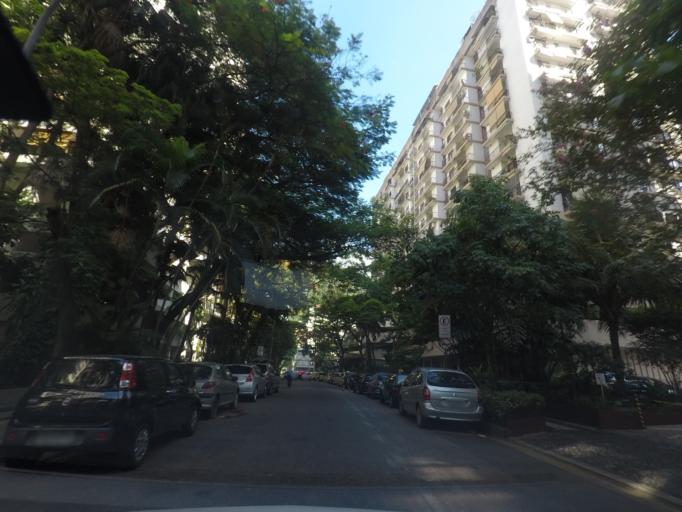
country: BR
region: Rio de Janeiro
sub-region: Rio De Janeiro
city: Rio de Janeiro
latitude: -22.9777
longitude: -43.2285
